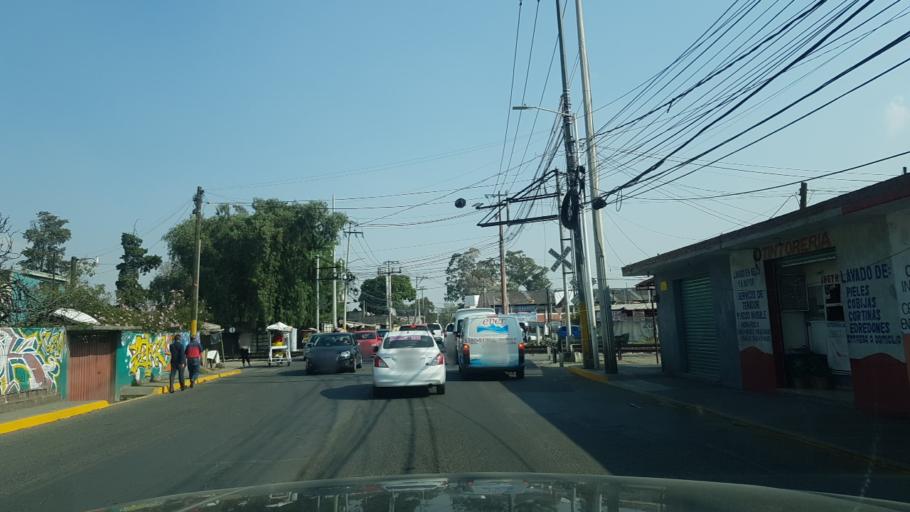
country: MX
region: Mexico
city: Santiago Teyahualco
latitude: 19.6620
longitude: -99.1292
